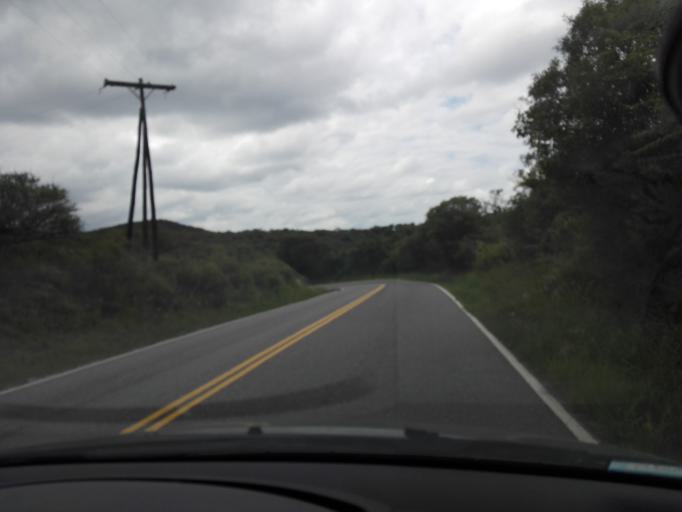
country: AR
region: Cordoba
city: Alta Gracia
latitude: -31.5960
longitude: -64.4921
